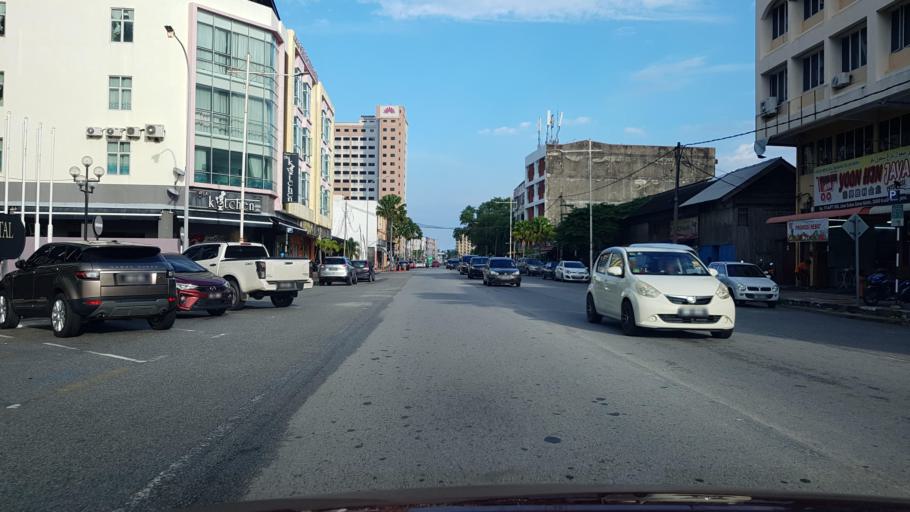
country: MY
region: Terengganu
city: Kuala Terengganu
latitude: 5.3349
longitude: 103.1463
